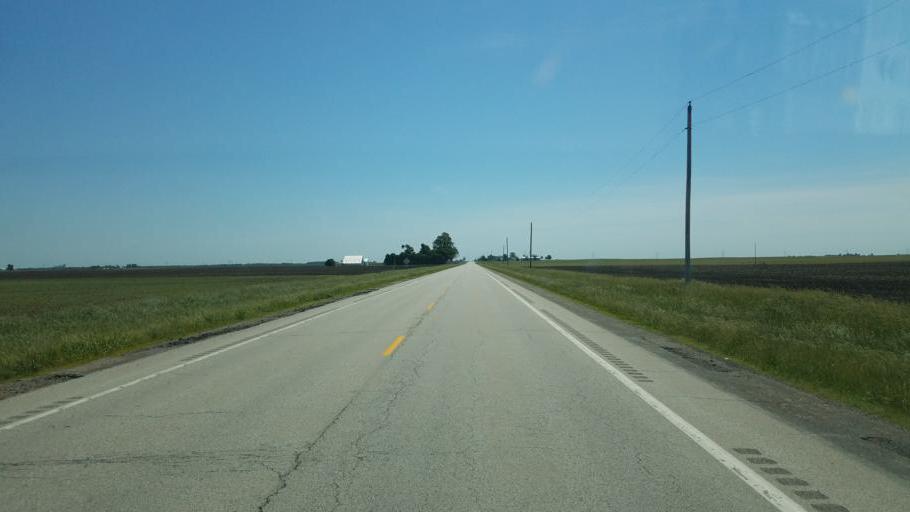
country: US
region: Illinois
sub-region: McLean County
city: Downs
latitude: 40.3120
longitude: -88.8612
